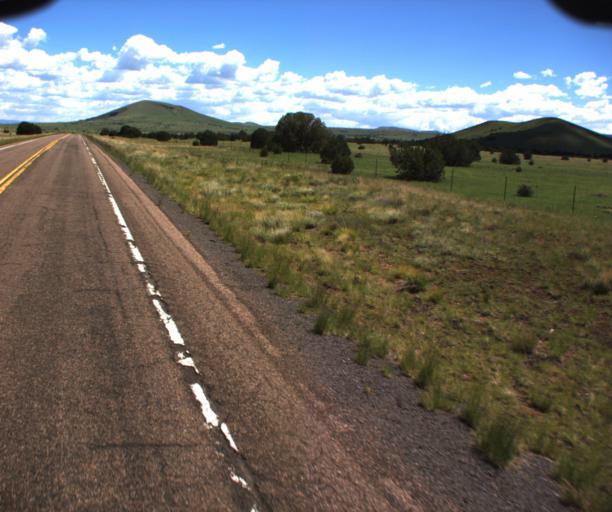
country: US
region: Arizona
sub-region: Apache County
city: Springerville
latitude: 34.2531
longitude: -109.5419
